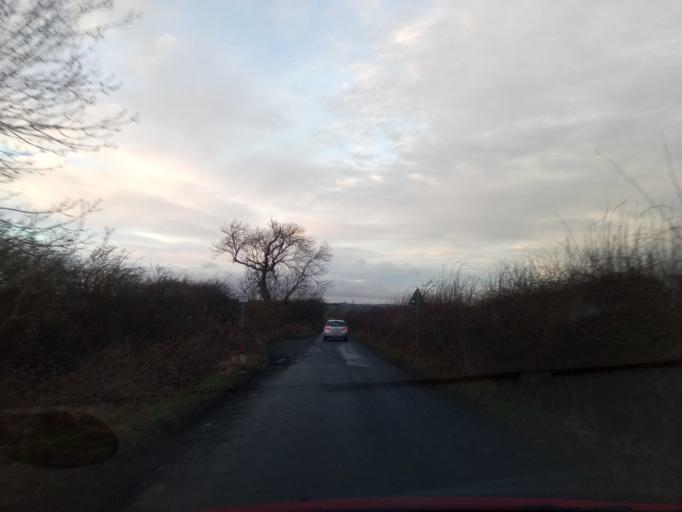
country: GB
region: England
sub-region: Northumberland
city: Ponteland
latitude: 55.0810
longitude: -1.7386
